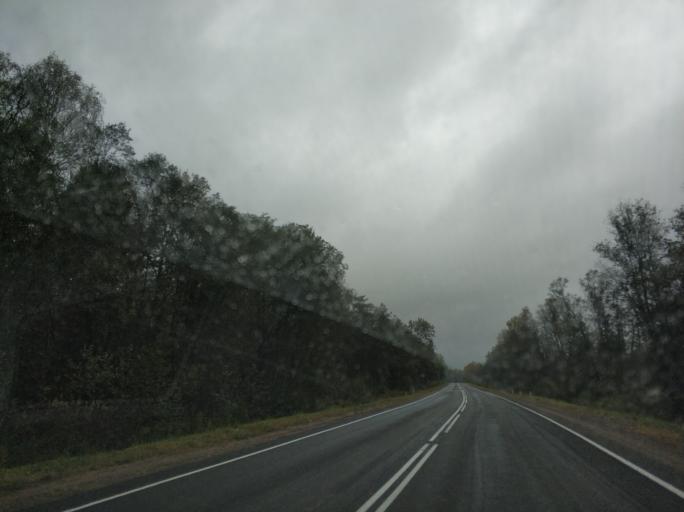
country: RU
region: Pskov
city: Sebezh
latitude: 56.2705
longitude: 28.5920
